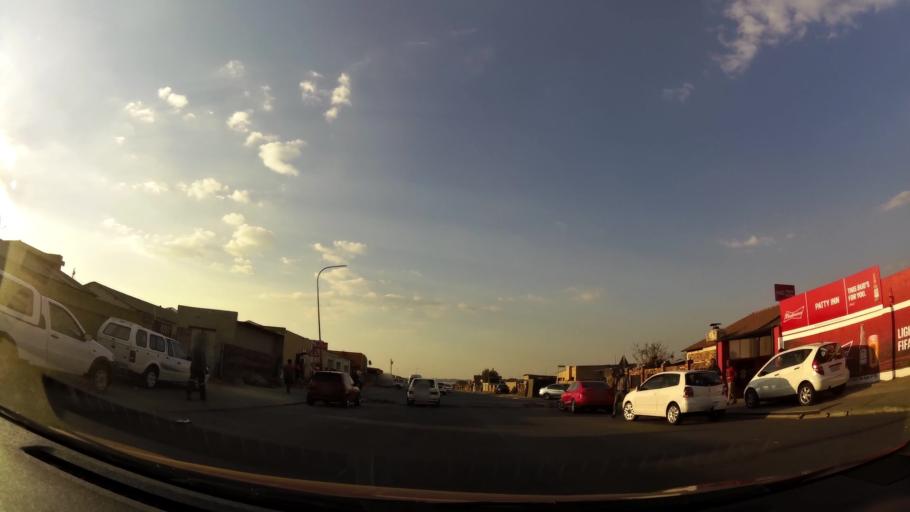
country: ZA
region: Gauteng
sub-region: City of Johannesburg Metropolitan Municipality
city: Roodepoort
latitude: -26.2140
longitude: 27.9019
